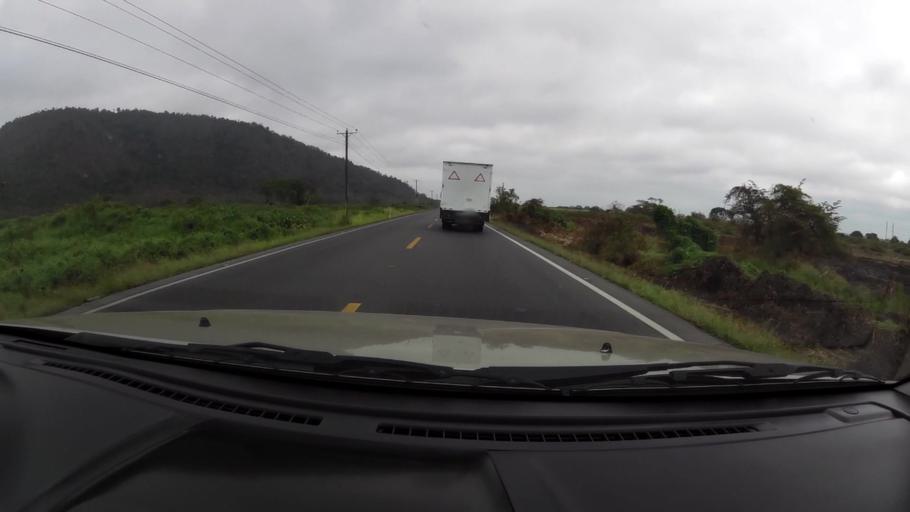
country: EC
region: Guayas
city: Naranjal
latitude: -2.4380
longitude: -79.6267
